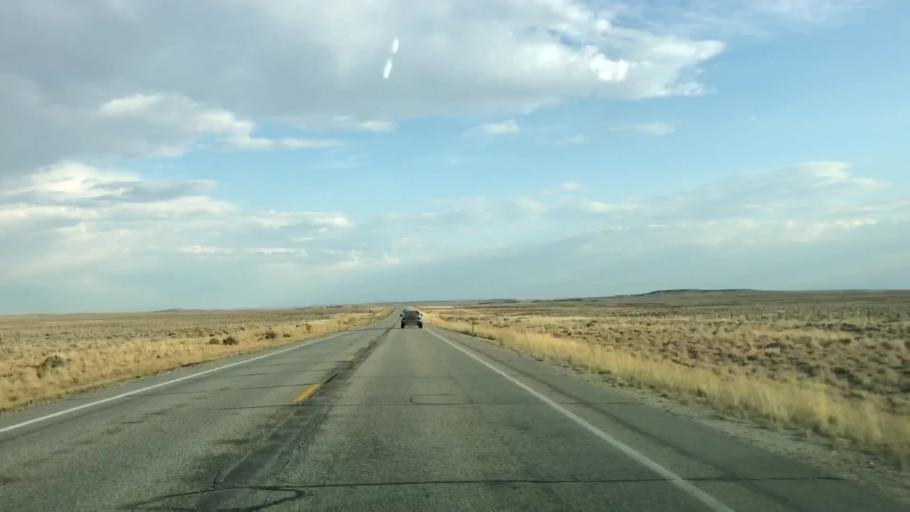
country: US
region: Wyoming
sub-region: Sublette County
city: Pinedale
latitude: 42.3850
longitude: -109.5370
